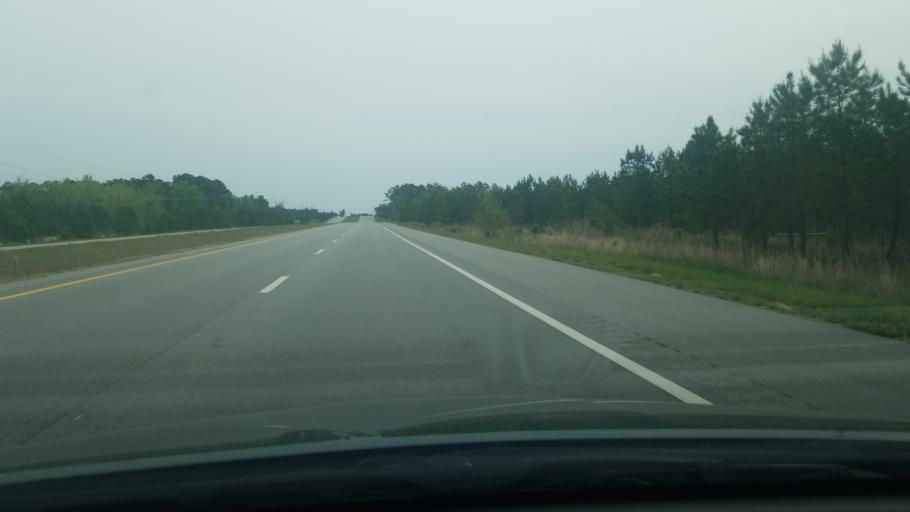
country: US
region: North Carolina
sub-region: Craven County
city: River Bend
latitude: 35.0465
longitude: -77.2172
